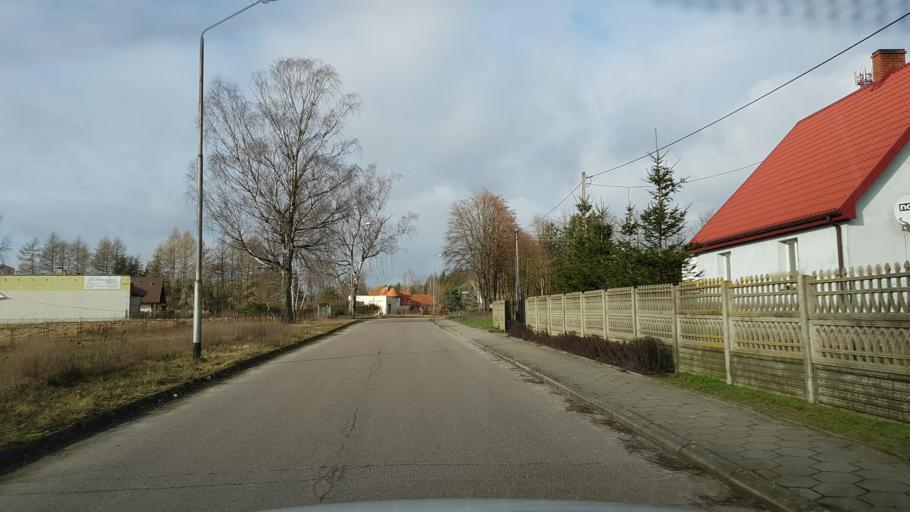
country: PL
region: West Pomeranian Voivodeship
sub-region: Powiat swidwinski
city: Rabino
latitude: 53.7753
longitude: 15.9647
